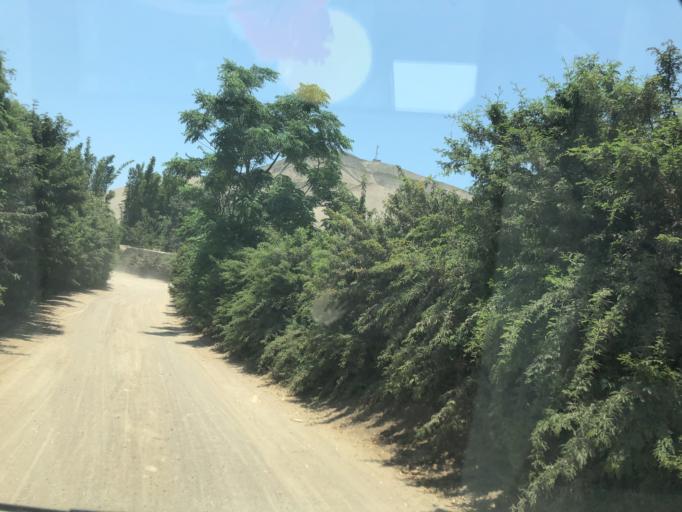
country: PE
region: Lima
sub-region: Provincia de Canete
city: Quilmana
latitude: -13.0039
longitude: -76.4530
